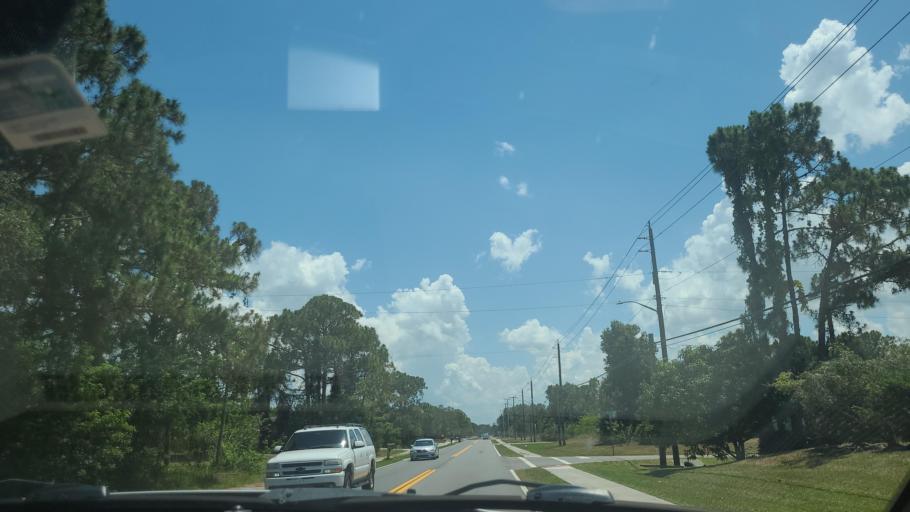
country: US
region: Florida
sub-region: Brevard County
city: Grant-Valkaria
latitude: 27.9467
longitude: -80.6279
